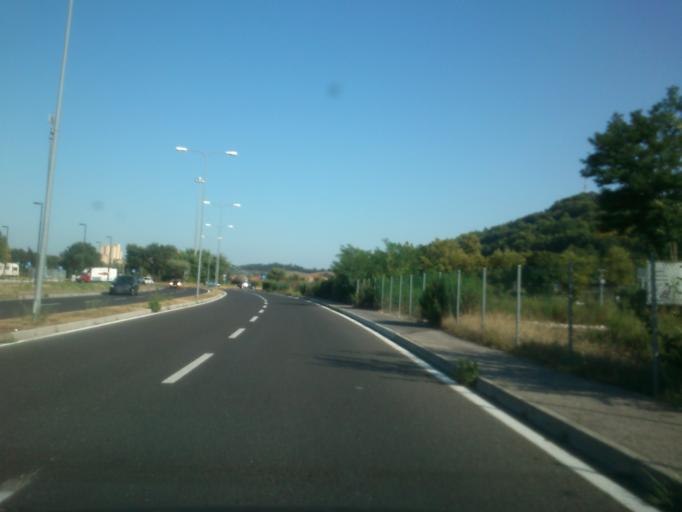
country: IT
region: The Marches
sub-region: Provincia di Pesaro e Urbino
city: Pesaro
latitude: 43.8922
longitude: 12.8860
